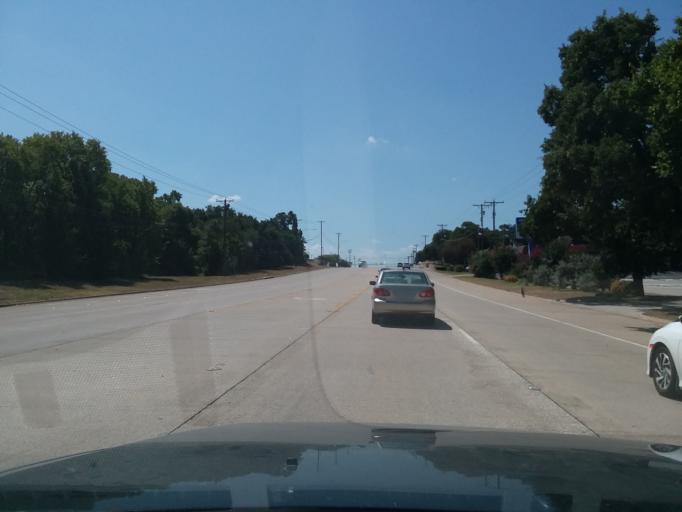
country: US
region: Texas
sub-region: Tarrant County
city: Euless
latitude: 32.8556
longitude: -97.1000
